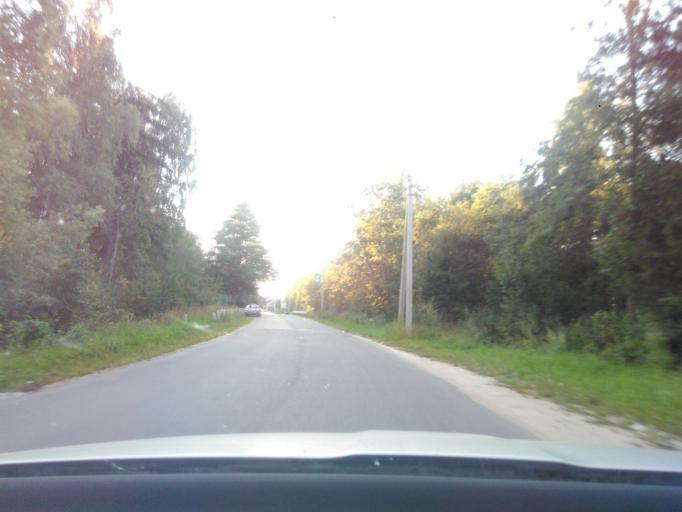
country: RU
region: Tverskaya
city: Konakovo
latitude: 56.7488
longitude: 36.7618
